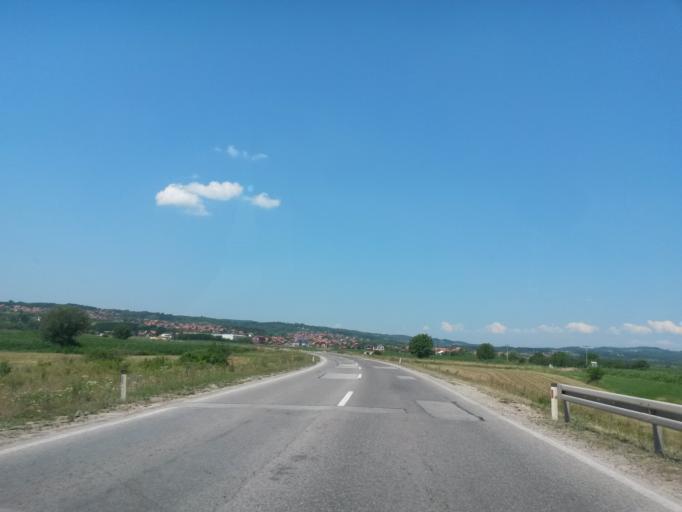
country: BA
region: Federation of Bosnia and Herzegovina
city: Odzak
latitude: 44.9728
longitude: 18.2965
